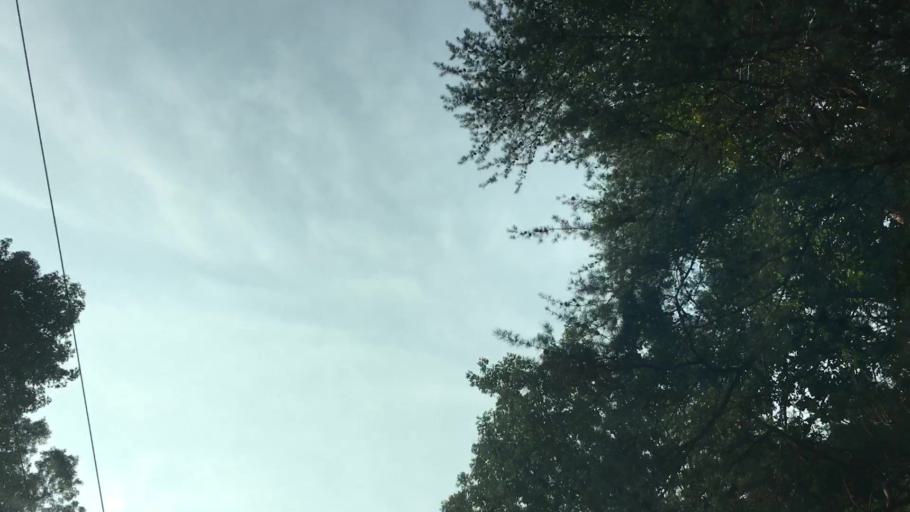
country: US
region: Alabama
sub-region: Bibb County
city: Woodstock
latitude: 33.2185
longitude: -87.1165
